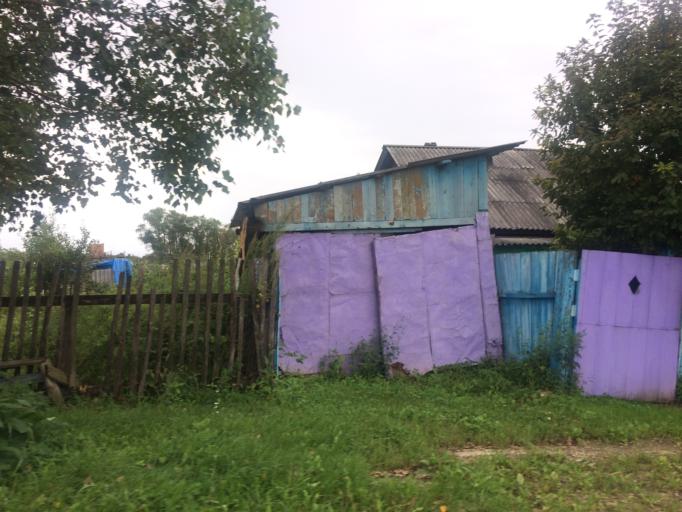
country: RU
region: Primorskiy
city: Lazo
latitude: 45.8296
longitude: 133.6195
